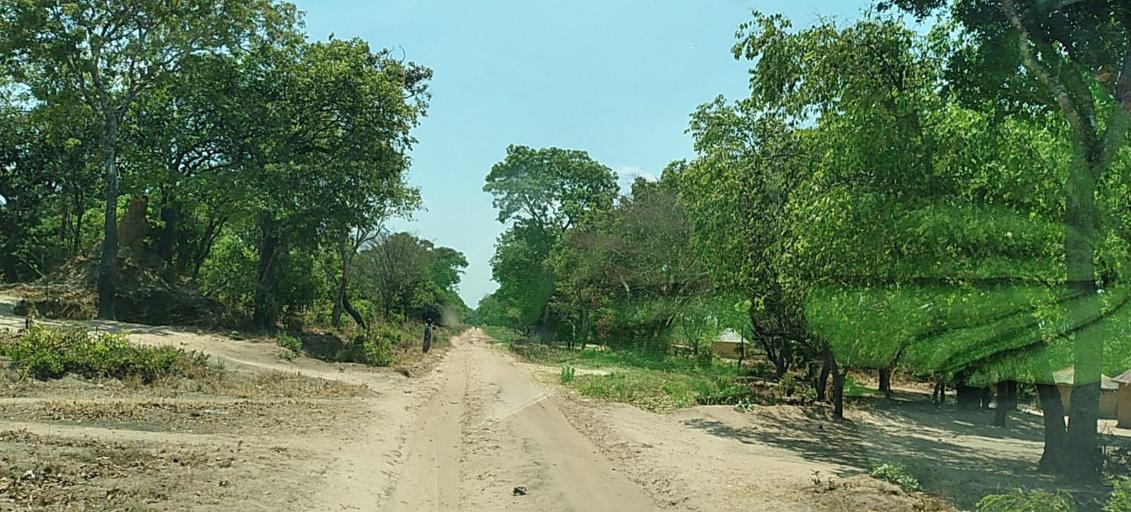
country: CD
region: Katanga
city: Kolwezi
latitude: -11.3689
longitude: 25.2111
